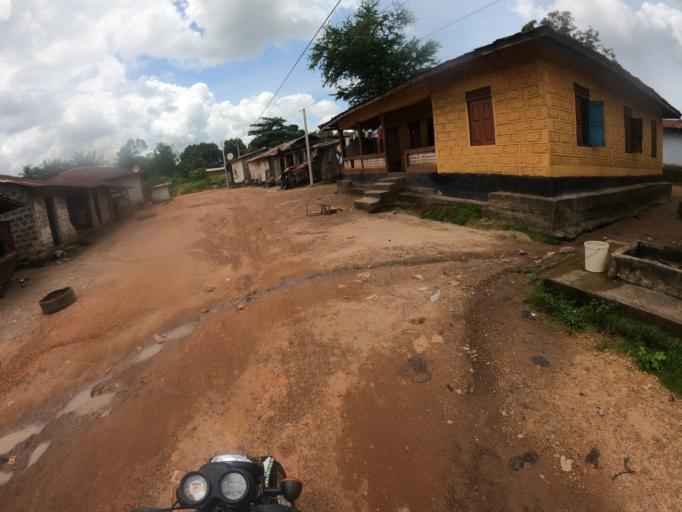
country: SL
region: Northern Province
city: Makeni
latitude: 8.8910
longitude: -12.0536
